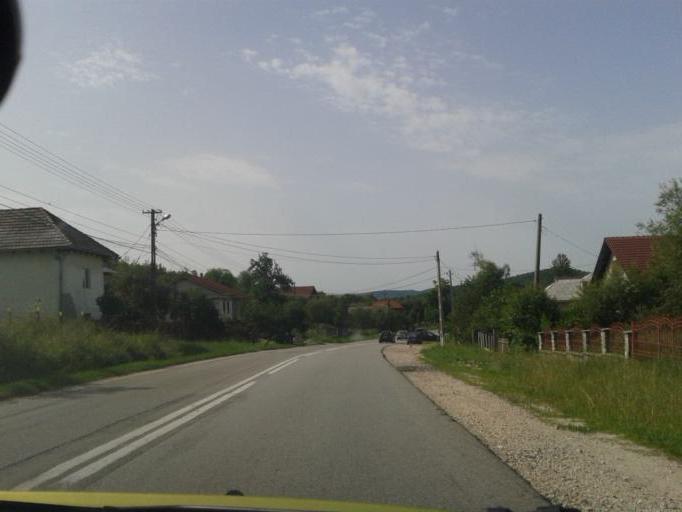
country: RO
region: Valcea
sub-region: Comuna Pietrari
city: Pietrarii de Sus
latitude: 45.1172
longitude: 24.1161
